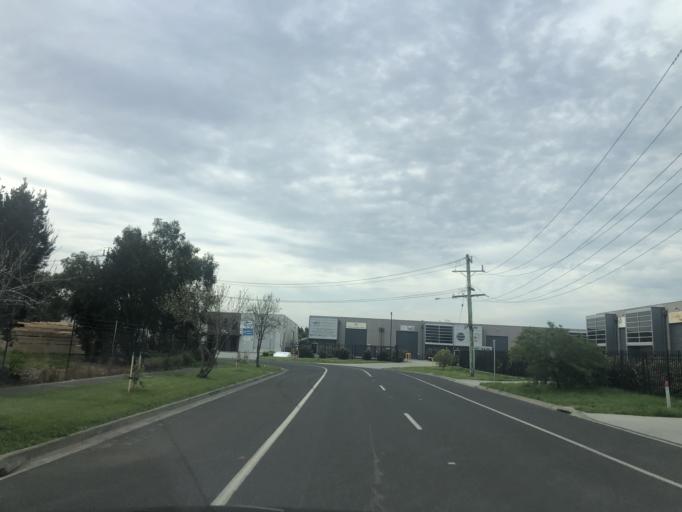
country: AU
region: Victoria
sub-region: Casey
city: Hallam
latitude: -38.0202
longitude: 145.2790
